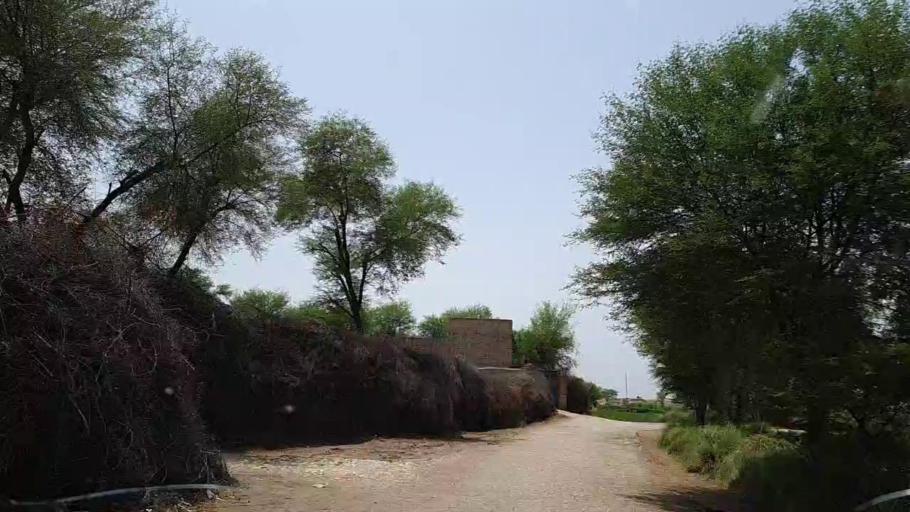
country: PK
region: Sindh
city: Tharu Shah
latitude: 26.9961
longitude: 68.0813
